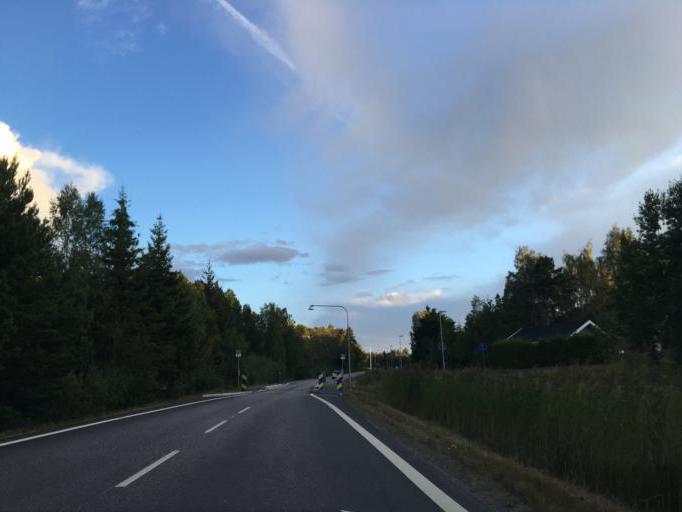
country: SE
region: Soedermanland
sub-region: Eskilstuna Kommun
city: Torshalla
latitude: 59.4331
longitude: 16.4587
